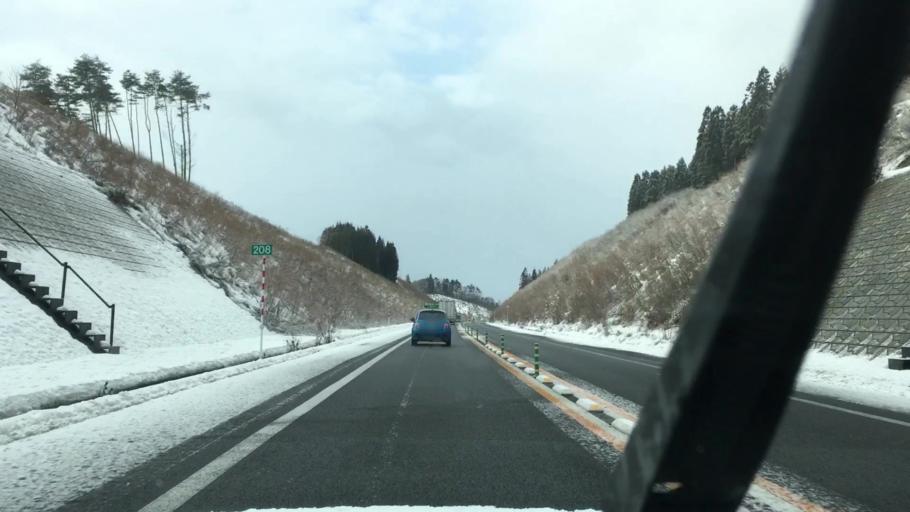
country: JP
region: Akita
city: Takanosu
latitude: 40.2144
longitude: 140.4207
